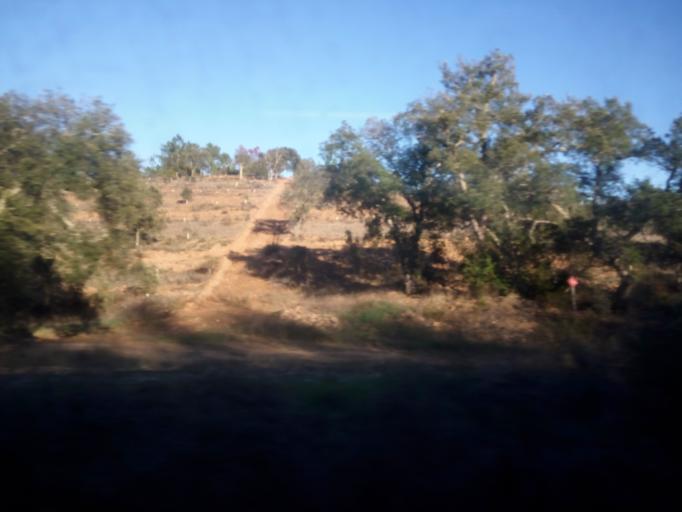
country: PT
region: Beja
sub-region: Odemira
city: Odemira
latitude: 37.5335
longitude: -8.4805
